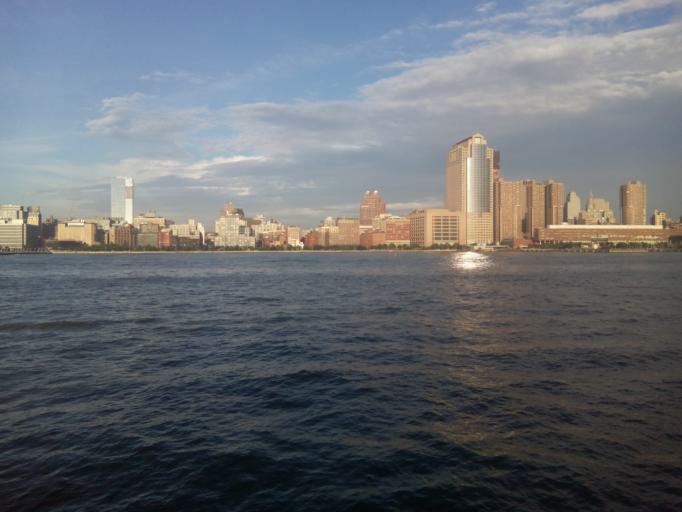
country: US
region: New York
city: New York City
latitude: 40.7251
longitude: -74.0206
